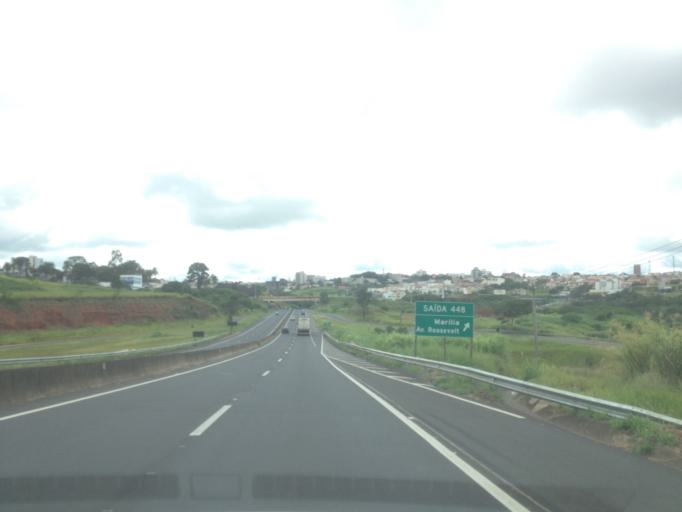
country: BR
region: Sao Paulo
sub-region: Marilia
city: Marilia
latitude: -22.2299
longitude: -49.9498
